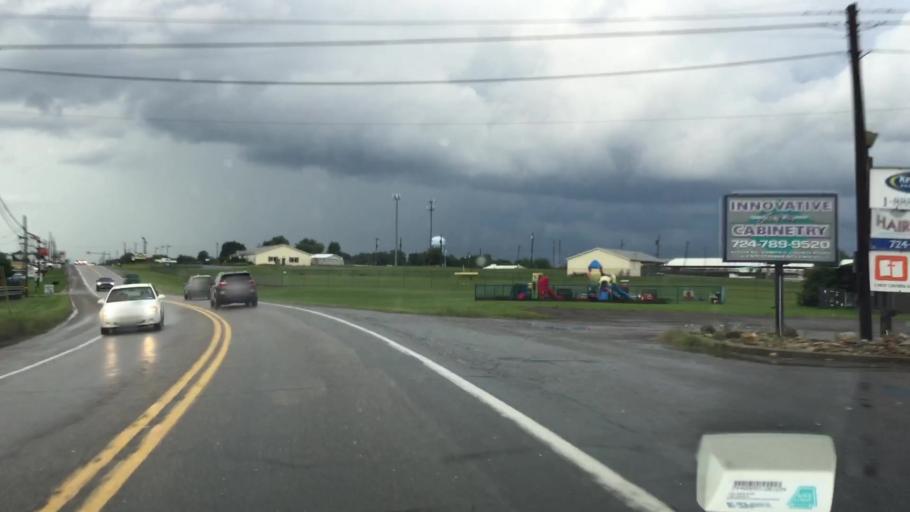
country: US
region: Pennsylvania
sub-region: Butler County
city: Meridian
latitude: 40.8555
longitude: -79.9771
